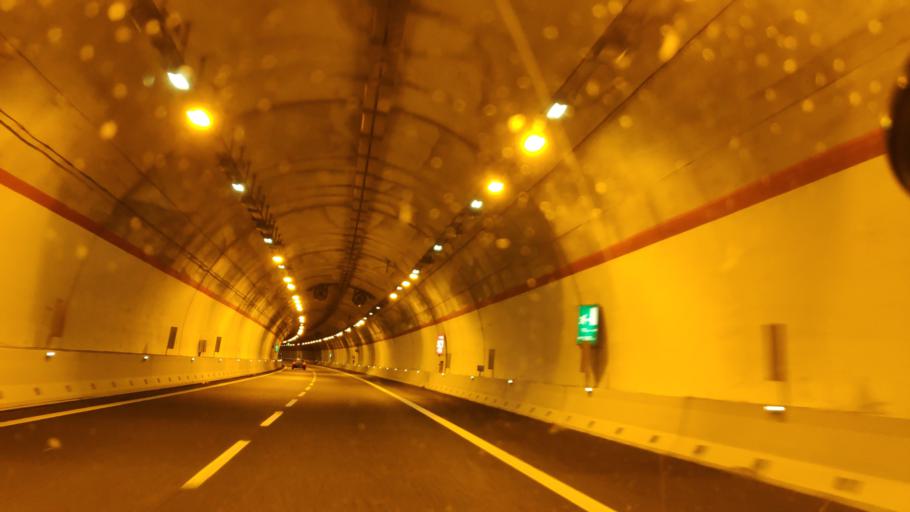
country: IT
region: Campania
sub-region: Provincia di Salerno
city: Casalbuono
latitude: 40.2131
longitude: 15.6733
